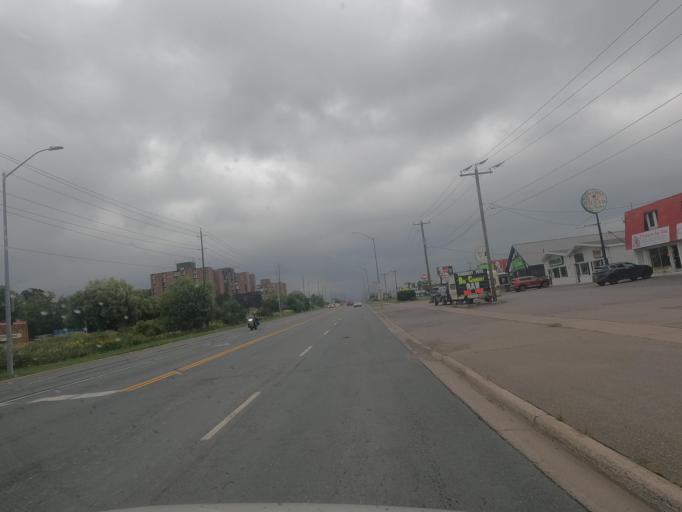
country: CA
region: Ontario
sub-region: Algoma
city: Sault Ste. Marie
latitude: 46.5124
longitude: -84.2951
